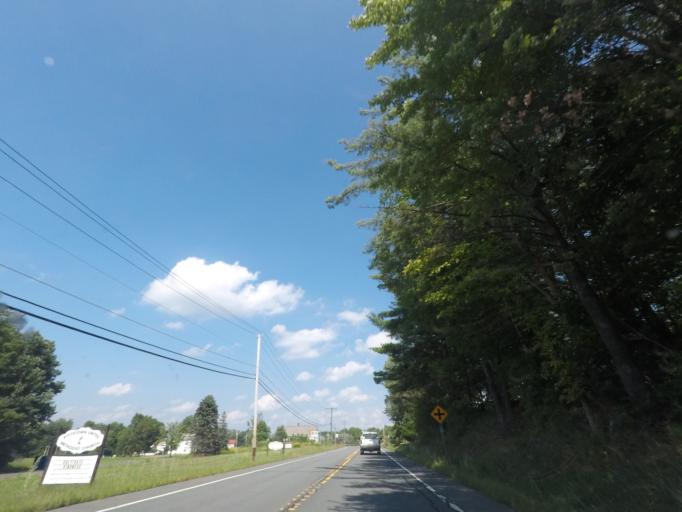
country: US
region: New York
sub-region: Rensselaer County
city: Hoosick Falls
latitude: 42.8325
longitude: -73.4877
